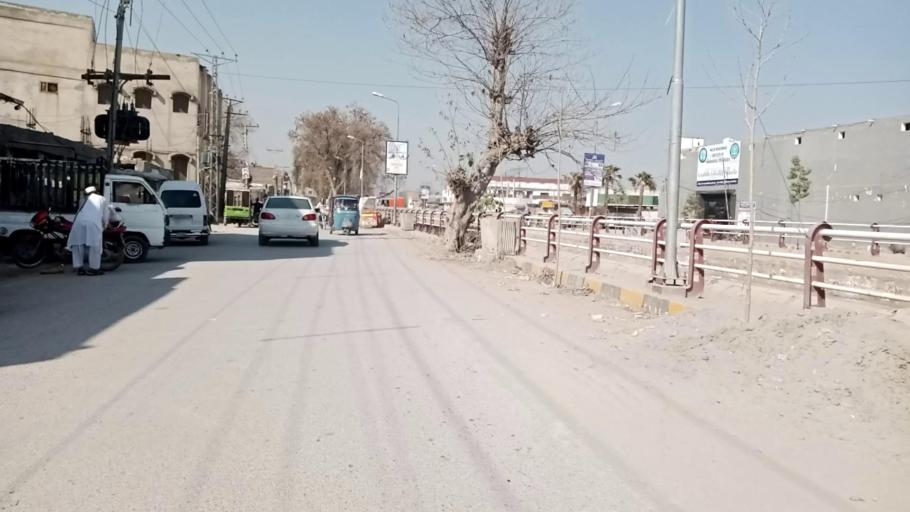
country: PK
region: Khyber Pakhtunkhwa
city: Peshawar
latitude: 33.9791
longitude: 71.5054
